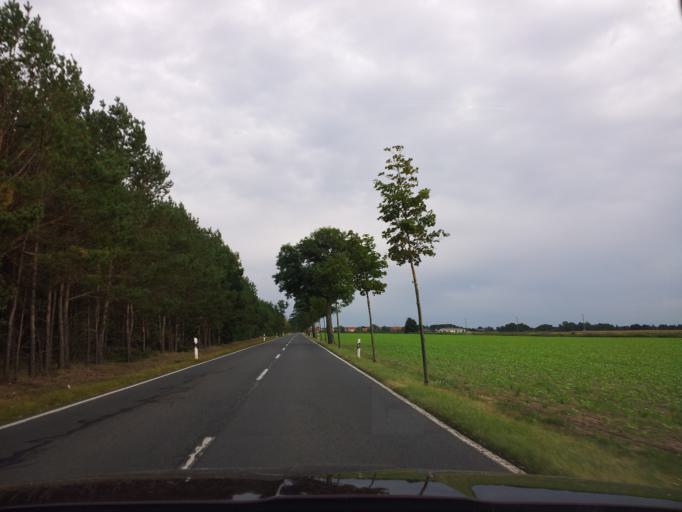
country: DE
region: Brandenburg
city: Beelitz
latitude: 52.1270
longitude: 13.0114
